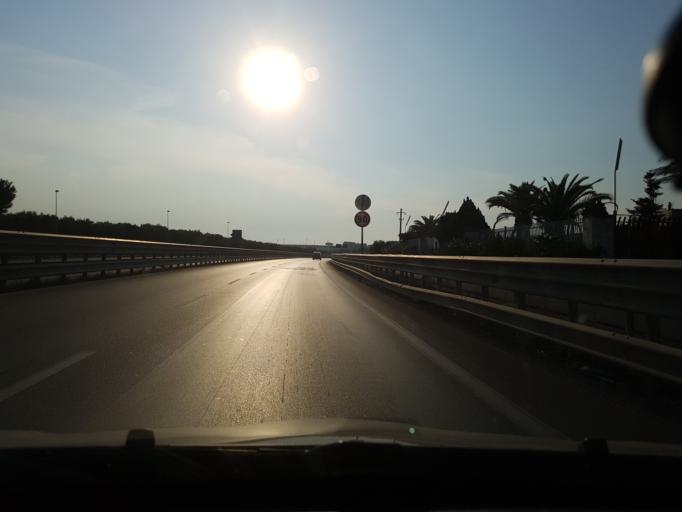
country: IT
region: Apulia
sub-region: Provincia di Foggia
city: Cerignola
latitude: 41.2755
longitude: 15.8719
